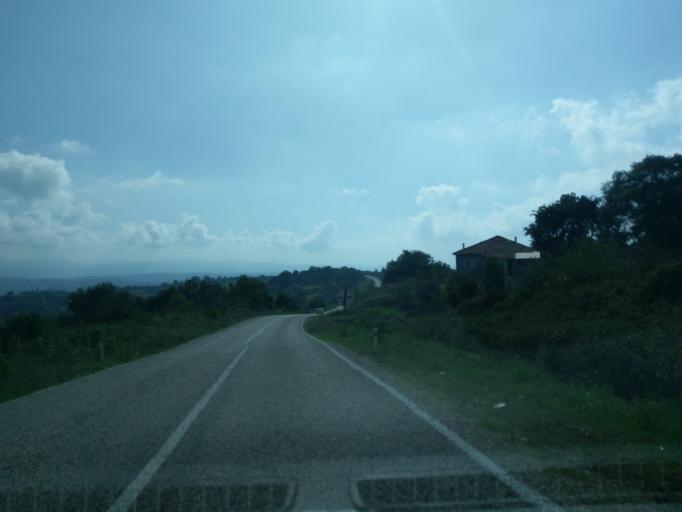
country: TR
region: Sinop
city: Erfelek
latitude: 41.9776
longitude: 34.8732
